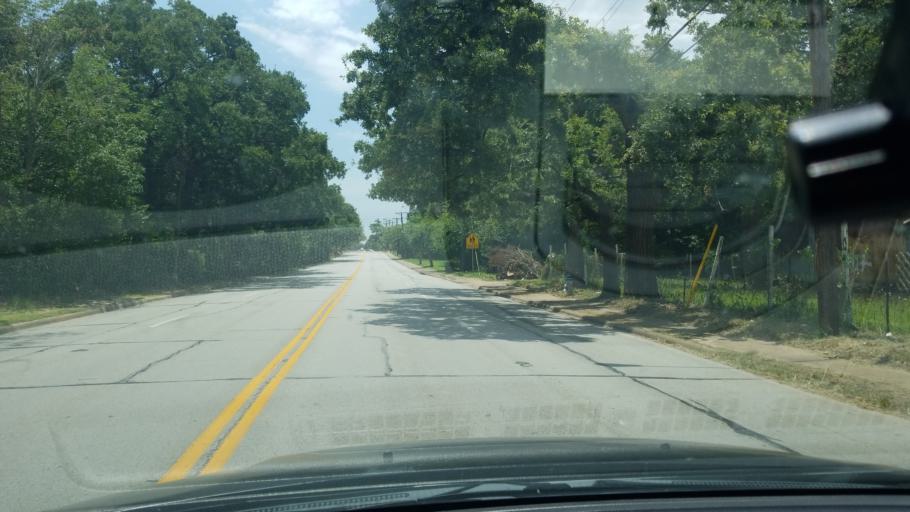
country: US
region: Texas
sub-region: Dallas County
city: Balch Springs
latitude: 32.7158
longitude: -96.6571
